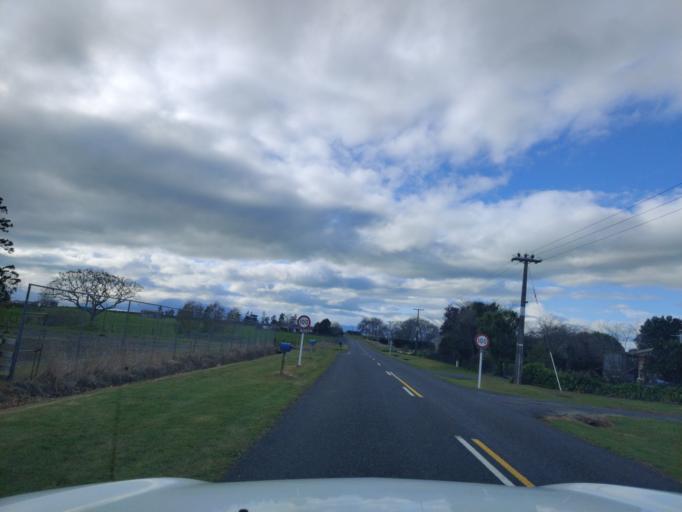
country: NZ
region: Waikato
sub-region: Hauraki District
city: Paeroa
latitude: -37.5895
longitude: 175.5033
